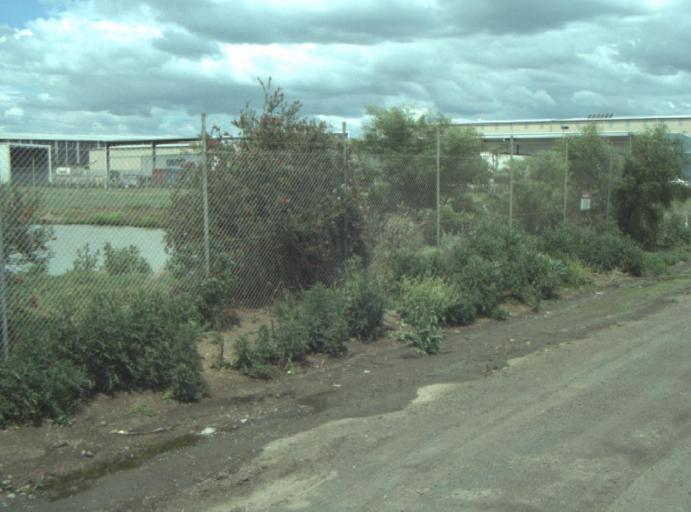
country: AU
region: Victoria
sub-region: Greater Geelong
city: Lara
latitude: -38.0514
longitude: 144.3798
